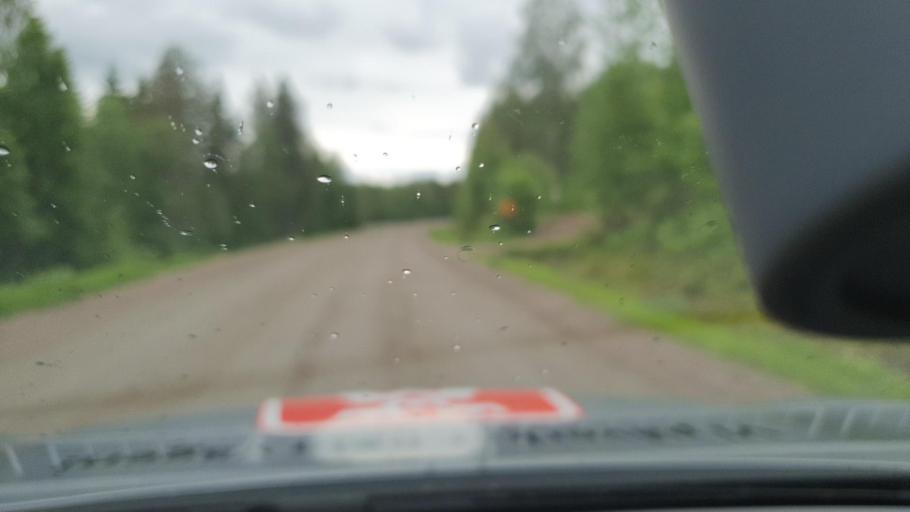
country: SE
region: Norrbotten
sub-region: Overtornea Kommun
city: OEvertornea
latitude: 66.4171
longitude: 23.5843
